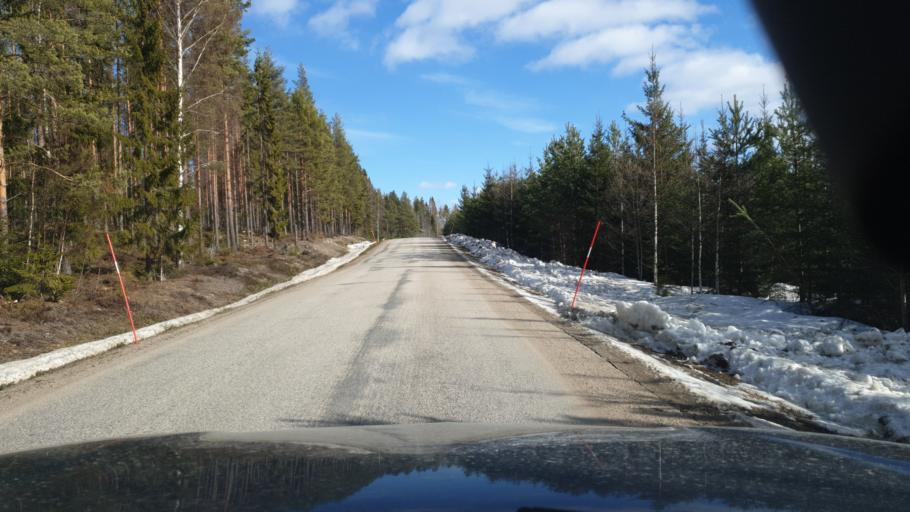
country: SE
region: Gaevleborg
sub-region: Ljusdals Kommun
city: Farila
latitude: 61.8467
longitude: 15.9633
